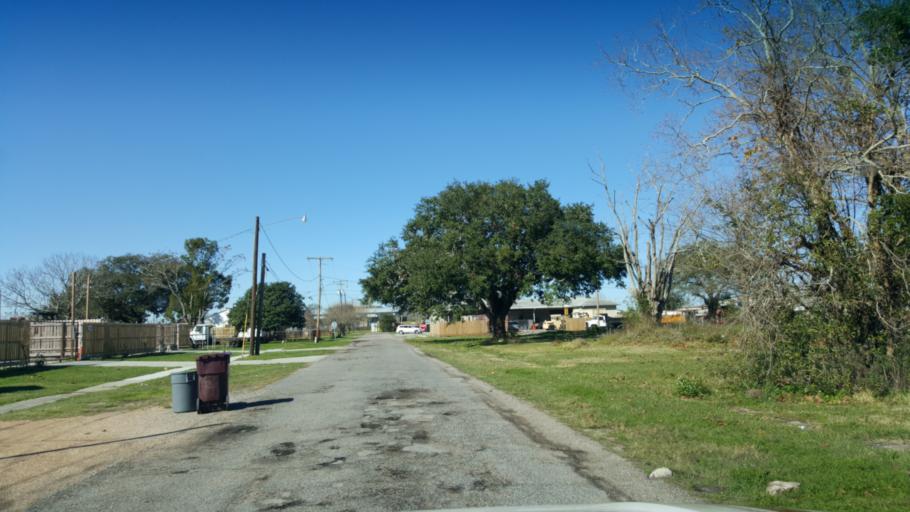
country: US
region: Louisiana
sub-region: Jefferson Parish
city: Kenner
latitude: 29.9757
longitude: -90.2532
